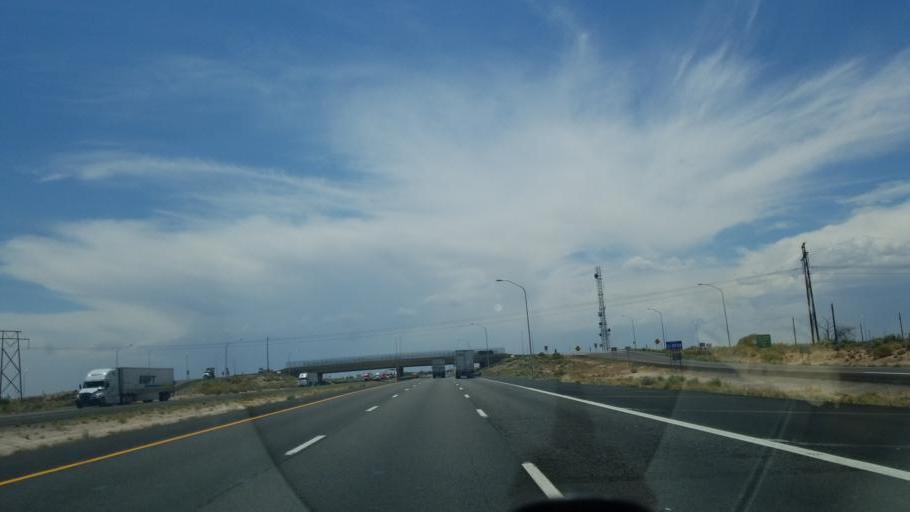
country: US
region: New Mexico
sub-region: Bernalillo County
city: South Valley
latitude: 35.0668
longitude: -106.7845
